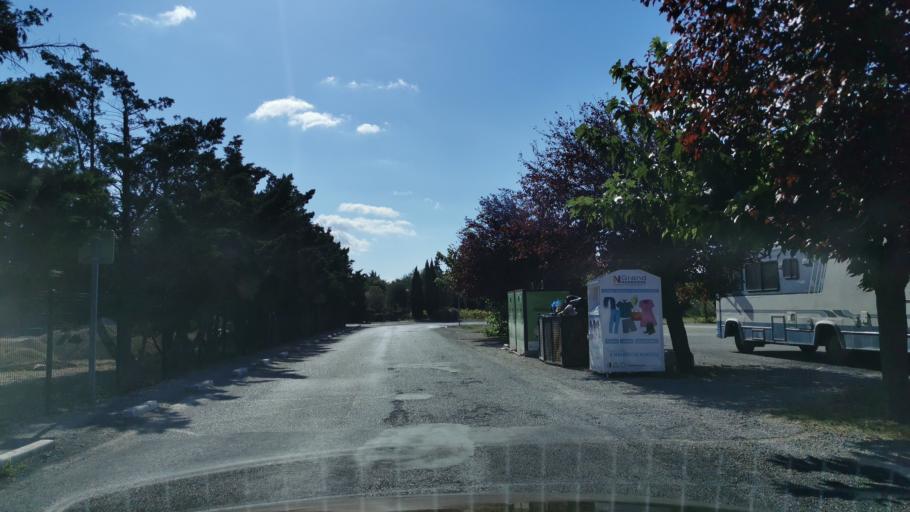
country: FR
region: Languedoc-Roussillon
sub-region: Departement de l'Aude
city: Ginestas
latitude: 43.2453
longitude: 2.8894
